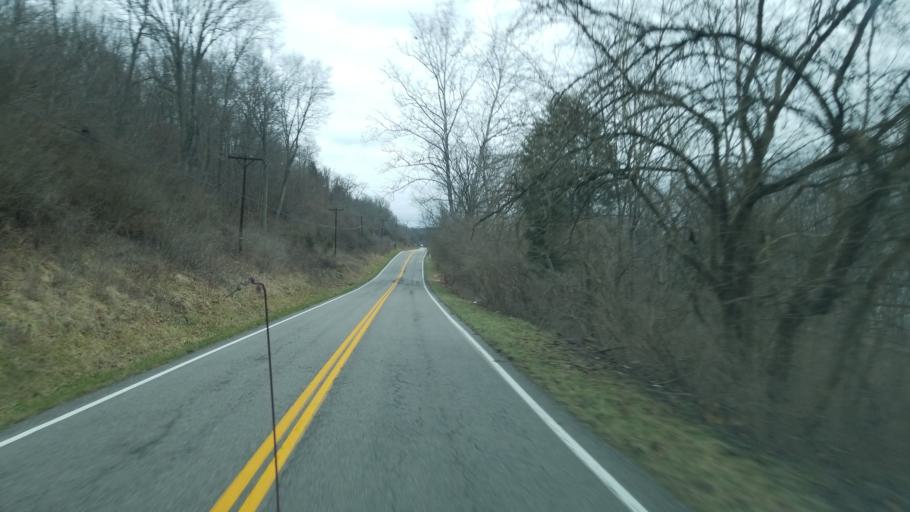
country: US
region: Ohio
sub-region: Clermont County
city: New Richmond
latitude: 38.9527
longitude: -84.2940
